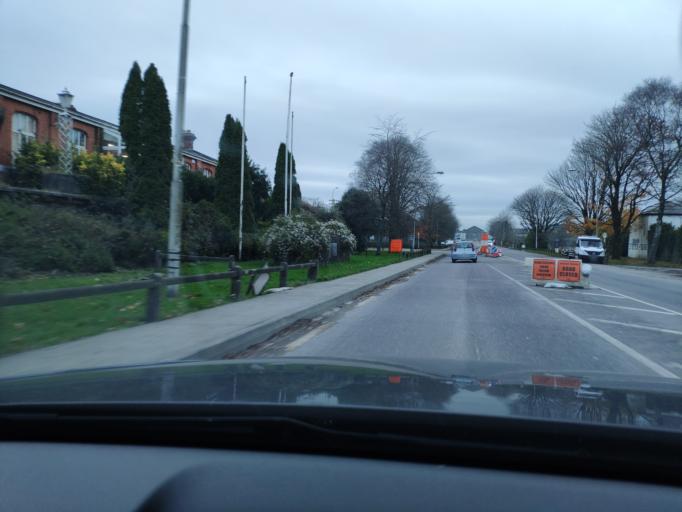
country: IE
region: Munster
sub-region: County Cork
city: Bandon
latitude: 51.7464
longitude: -8.7284
